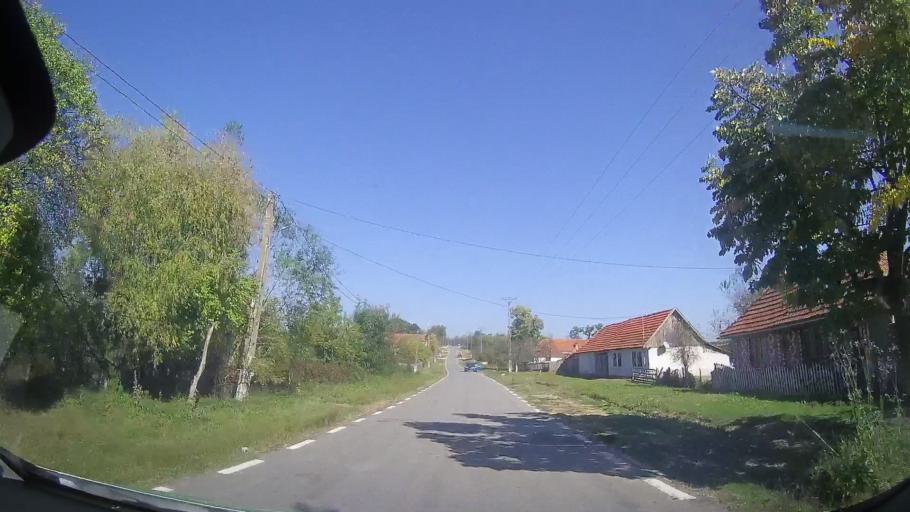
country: RO
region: Timis
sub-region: Comuna Ohaba Lunga
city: Ohaba Lunga
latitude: 45.9037
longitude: 21.9359
